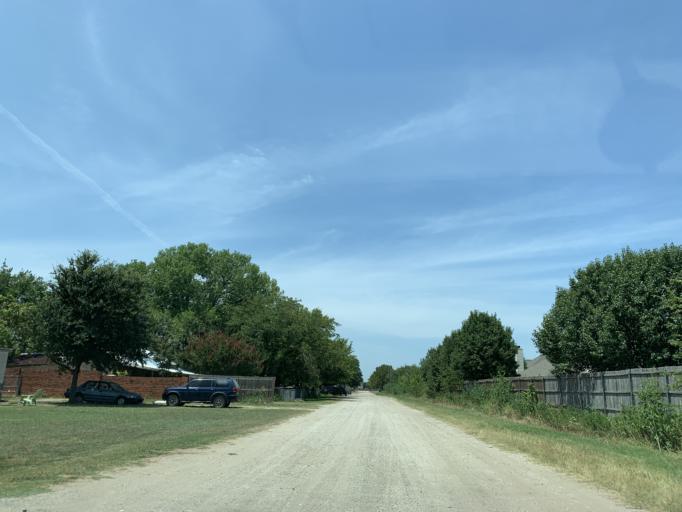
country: US
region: Texas
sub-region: Dallas County
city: Cedar Hill
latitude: 32.6435
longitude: -97.0256
